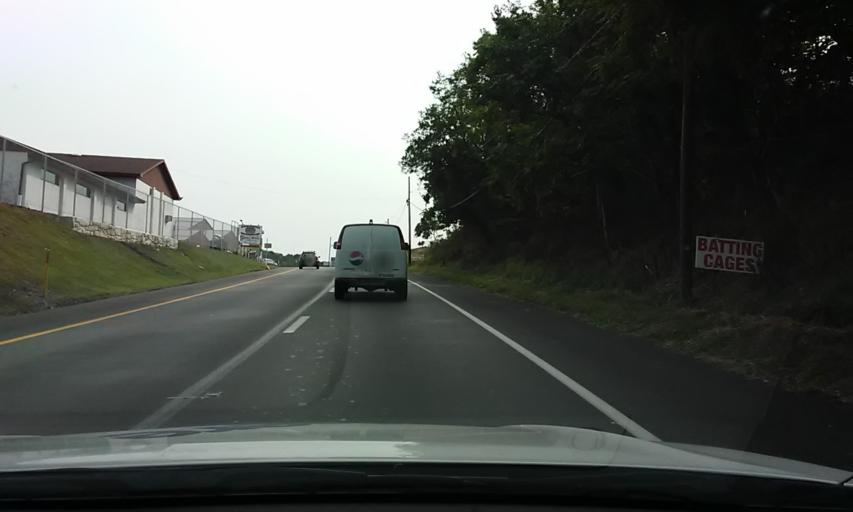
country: US
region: Pennsylvania
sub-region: Fayette County
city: Connellsville
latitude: 40.0075
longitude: -79.6021
